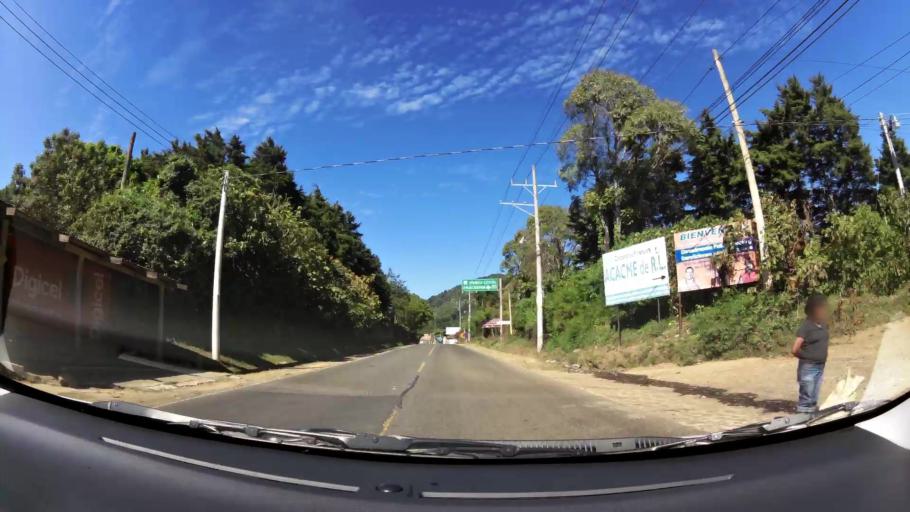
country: SV
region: Ahuachapan
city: Concepcion de Ataco
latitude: 13.8640
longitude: -89.7992
